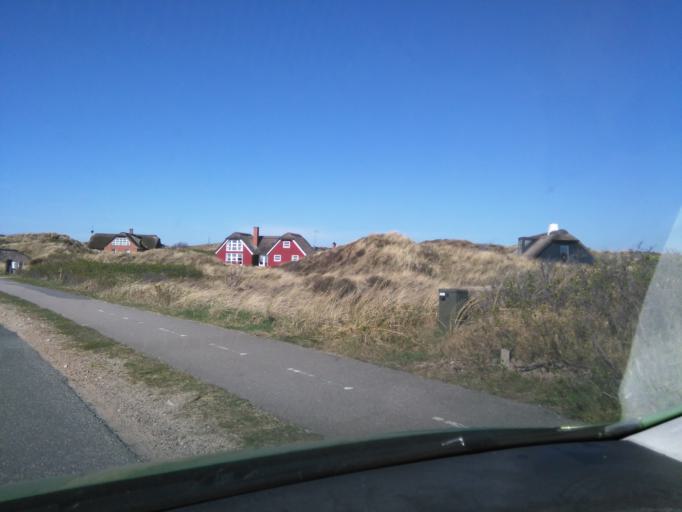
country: DK
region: South Denmark
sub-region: Varde Kommune
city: Oksbol
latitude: 55.5559
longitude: 8.0907
